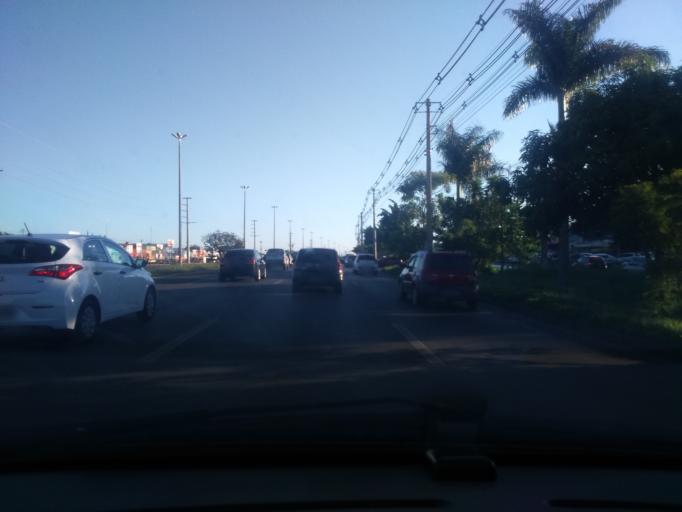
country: BR
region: Federal District
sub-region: Brasilia
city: Brasilia
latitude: -15.8726
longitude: -47.8227
